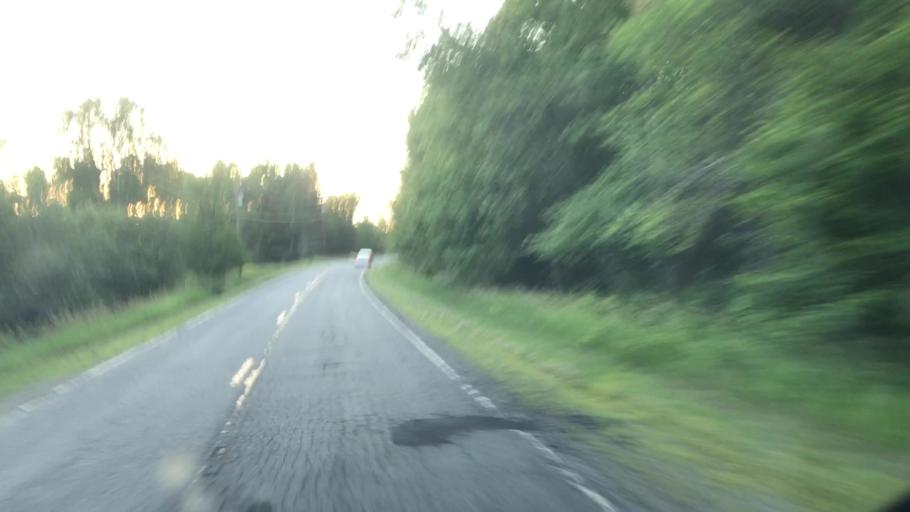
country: US
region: Maine
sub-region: Penobscot County
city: Medway
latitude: 45.5972
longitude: -68.2446
